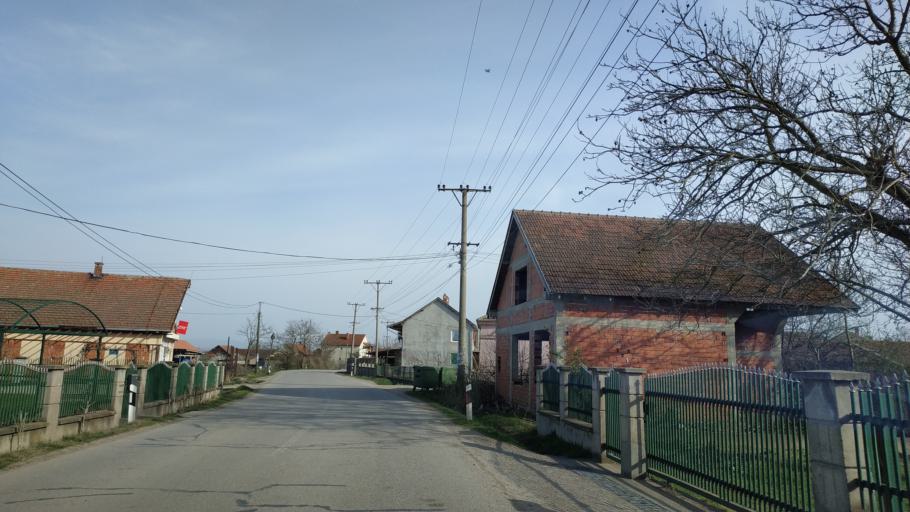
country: RS
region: Central Serbia
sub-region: Nisavski Okrug
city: Aleksinac
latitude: 43.5204
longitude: 21.6668
